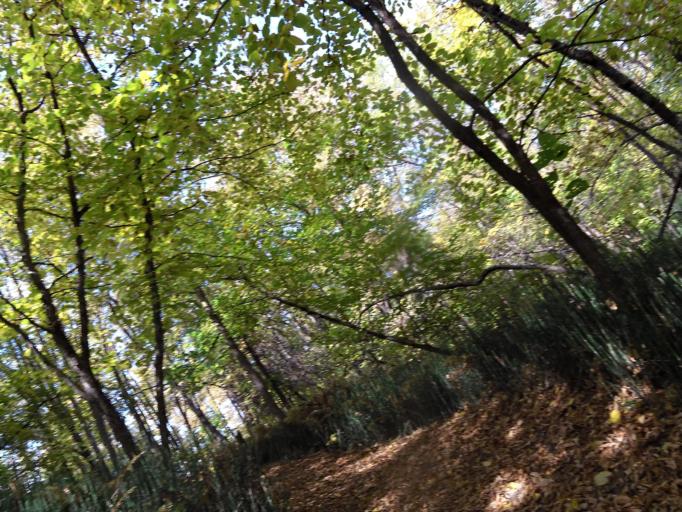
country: US
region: North Dakota
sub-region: Pembina County
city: Cavalier
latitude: 48.7762
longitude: -97.7376
